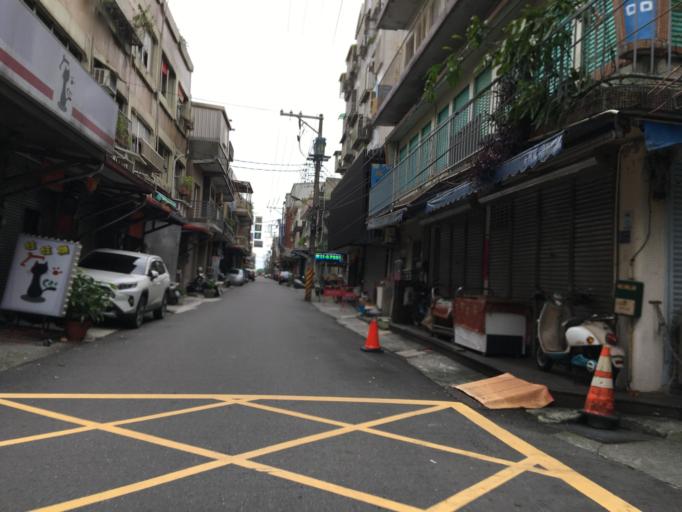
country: TW
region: Taiwan
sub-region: Yilan
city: Yilan
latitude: 24.5826
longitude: 121.8658
